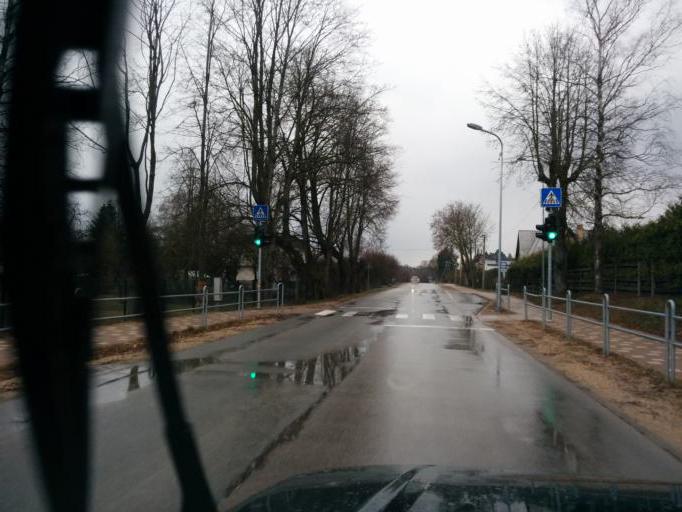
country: LV
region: Kekava
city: Kekava
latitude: 56.8704
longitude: 24.1851
